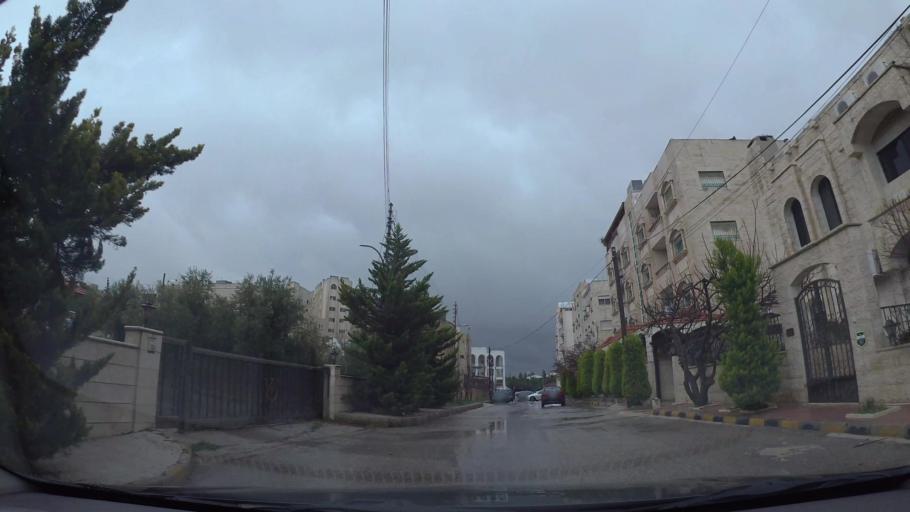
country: JO
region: Amman
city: Al Jubayhah
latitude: 32.0234
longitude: 35.8727
